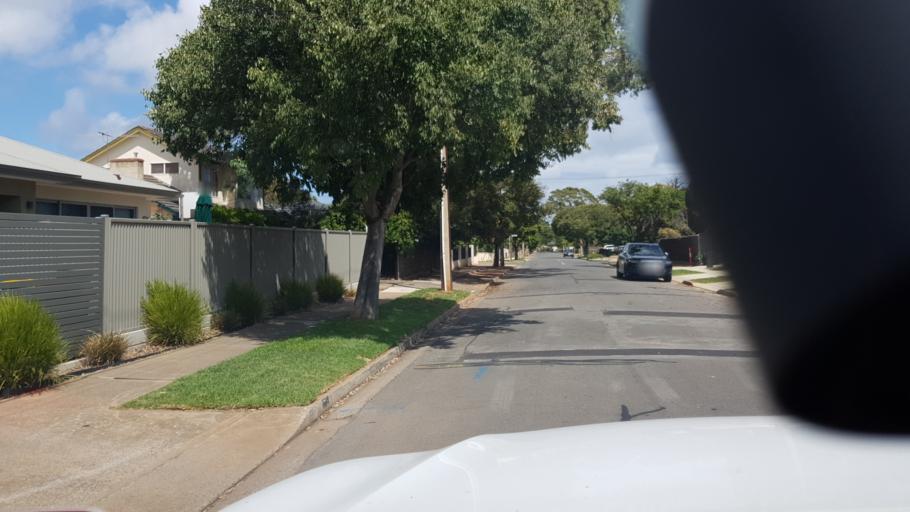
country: AU
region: South Australia
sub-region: Adelaide
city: Brighton
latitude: -35.0168
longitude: 138.5346
